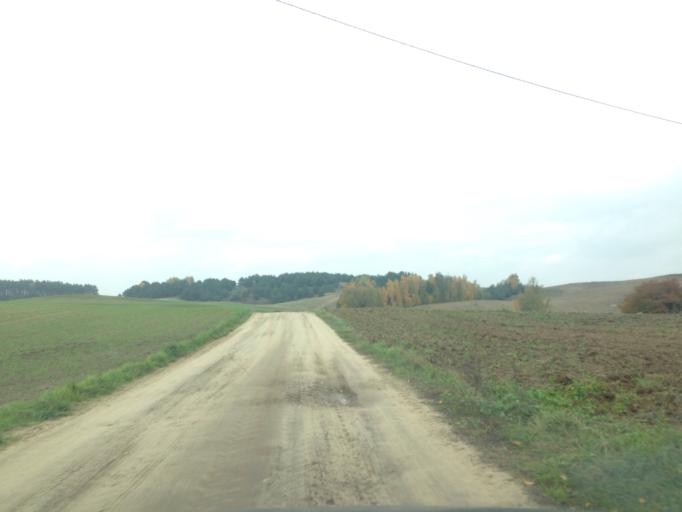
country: PL
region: Kujawsko-Pomorskie
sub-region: Powiat brodnicki
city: Brzozie
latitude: 53.3020
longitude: 19.6698
